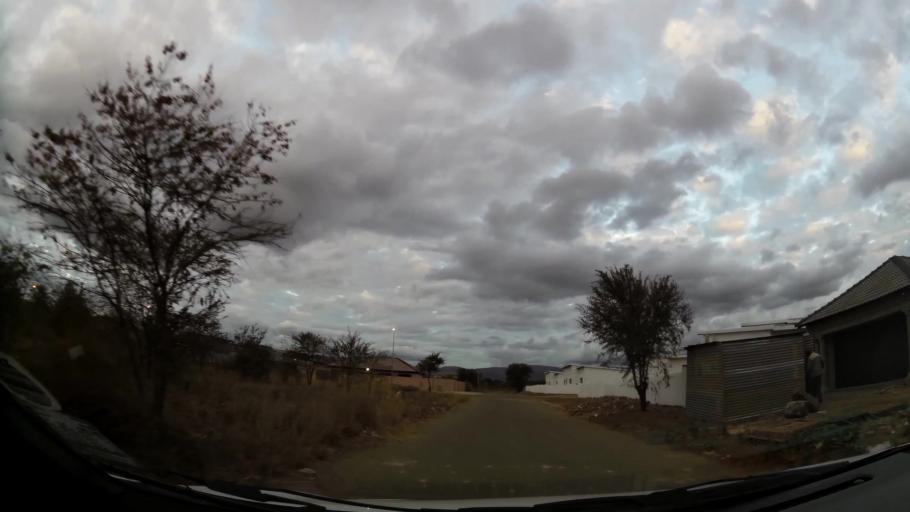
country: ZA
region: Limpopo
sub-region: Waterberg District Municipality
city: Mokopane
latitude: -24.1936
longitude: 28.9986
